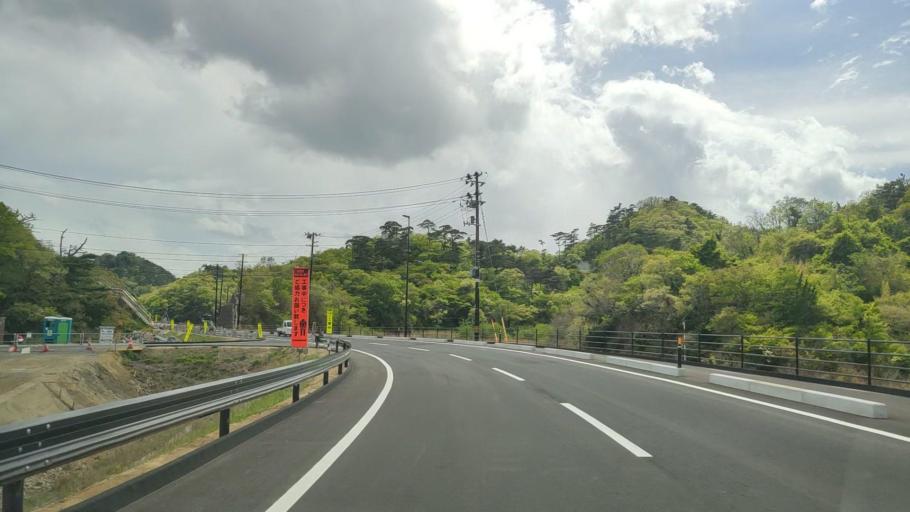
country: JP
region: Miyagi
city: Yamoto
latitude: 38.3516
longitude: 141.1552
